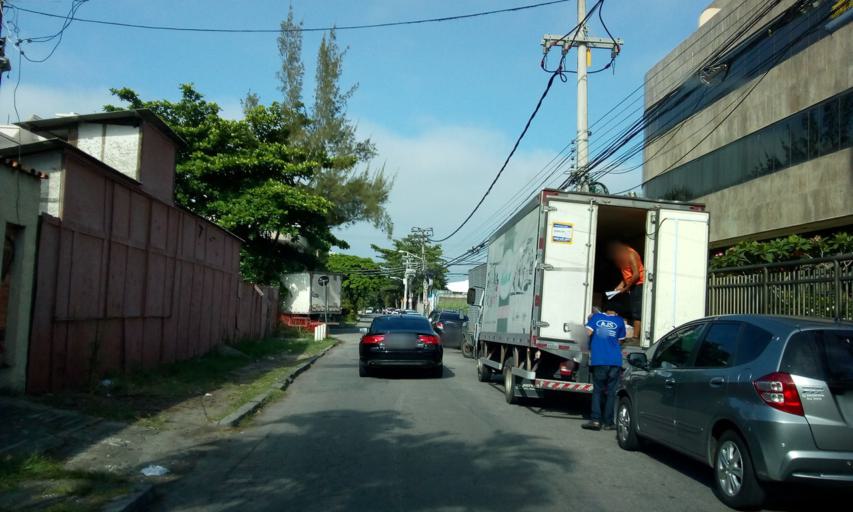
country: BR
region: Rio de Janeiro
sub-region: Nilopolis
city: Nilopolis
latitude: -23.0105
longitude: -43.4472
